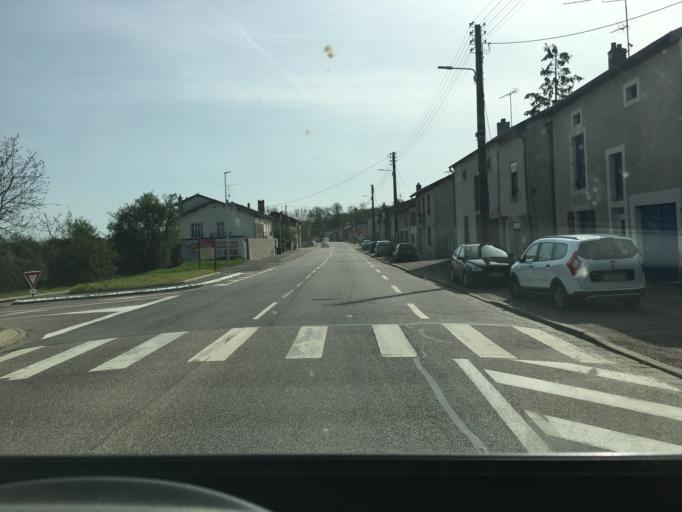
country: FR
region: Lorraine
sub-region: Departement de Meurthe-et-Moselle
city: Dommartin-les-Toul
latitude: 48.6713
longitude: 5.9038
